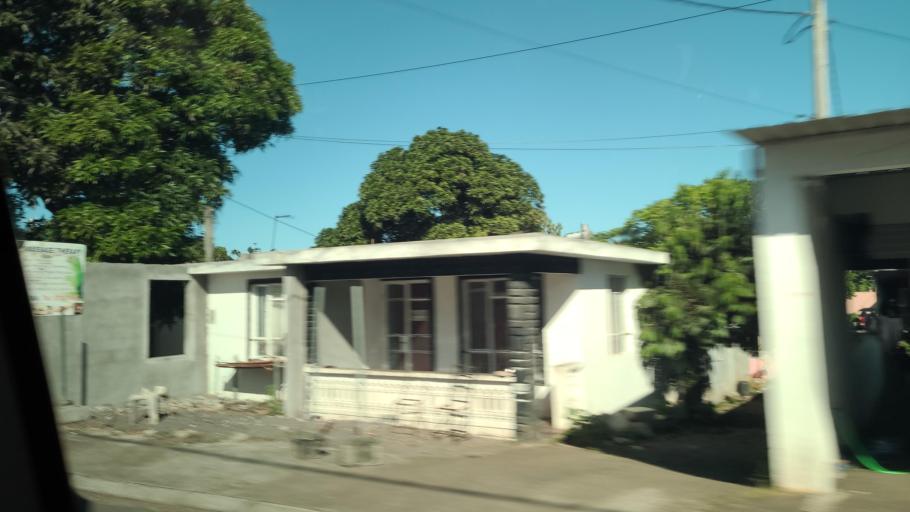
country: MU
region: Flacq
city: Poste de Flacq
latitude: -20.1695
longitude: 57.7331
